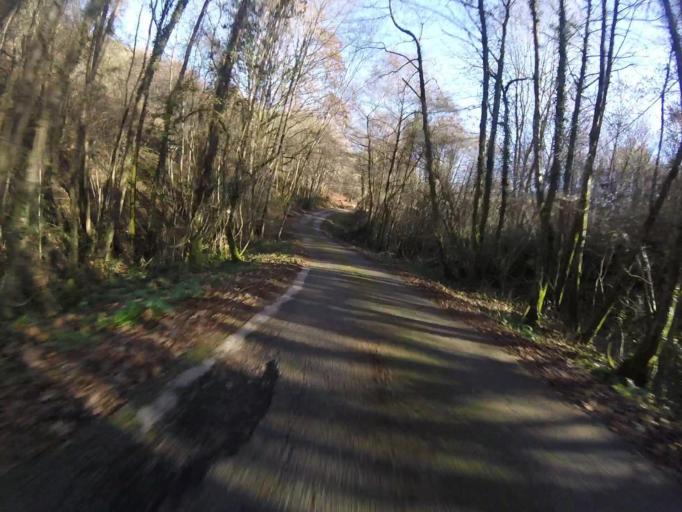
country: ES
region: Navarre
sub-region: Provincia de Navarra
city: Bera
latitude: 43.2962
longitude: -1.6521
